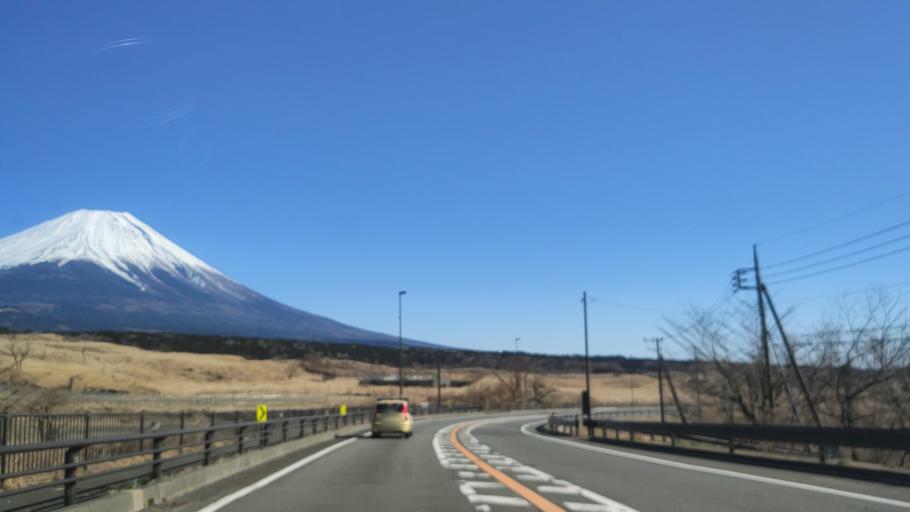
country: JP
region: Yamanashi
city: Fujikawaguchiko
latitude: 35.4259
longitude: 138.5922
